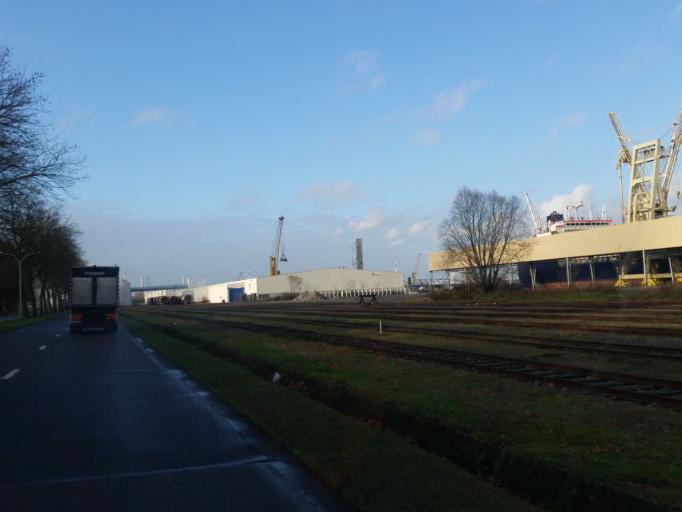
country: BE
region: Flanders
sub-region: Provincie Antwerpen
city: Antwerpen
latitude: 51.2425
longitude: 4.3963
